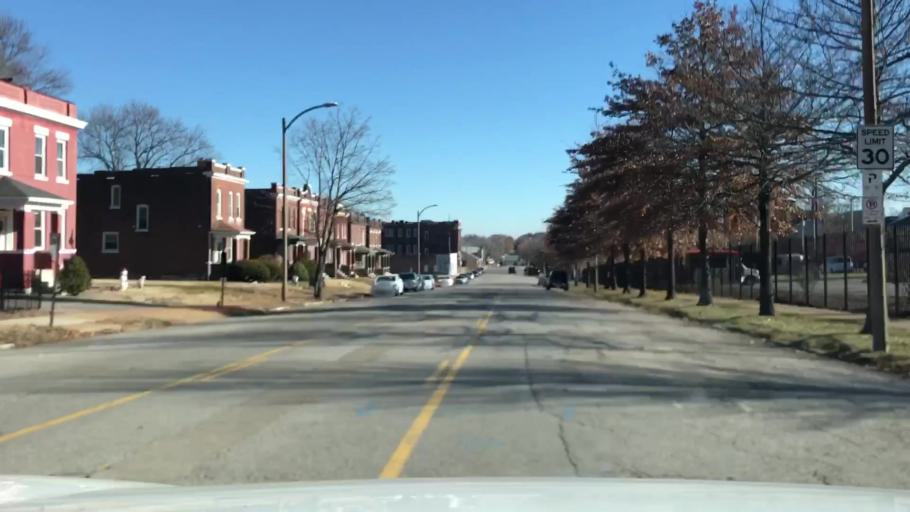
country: US
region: Missouri
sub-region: City of Saint Louis
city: St. Louis
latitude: 38.6203
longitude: -90.2356
